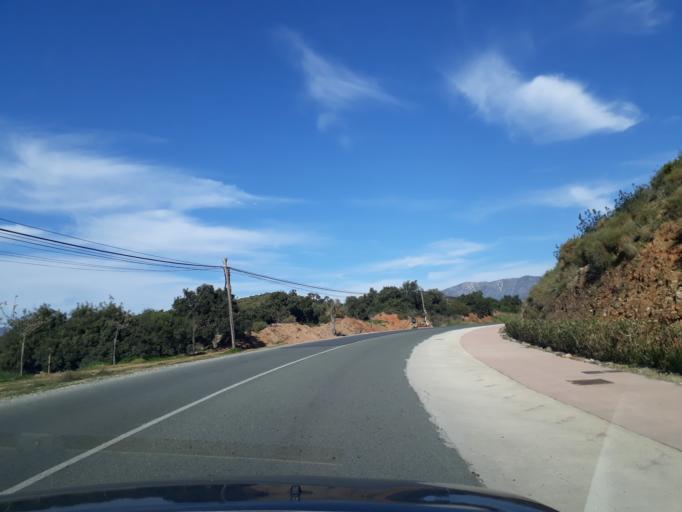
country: ES
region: Andalusia
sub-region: Provincia de Malaga
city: Fuengirola
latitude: 36.5115
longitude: -4.6878
